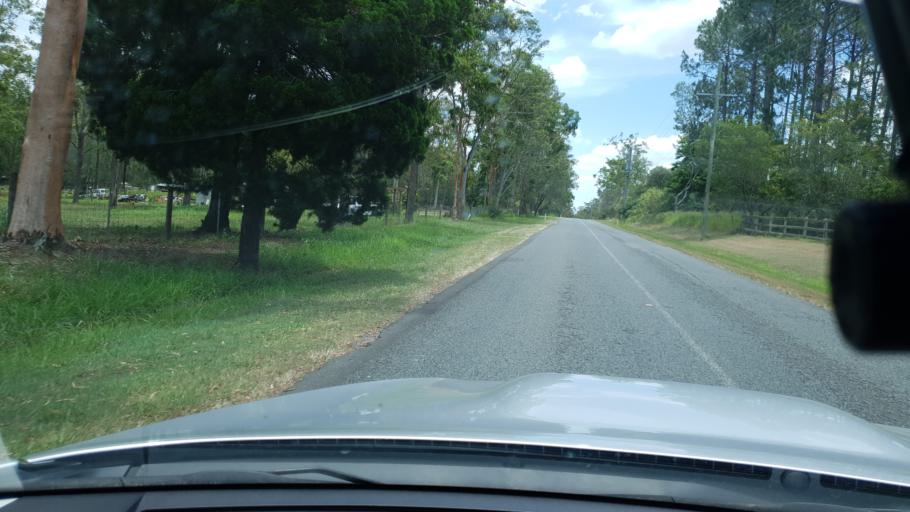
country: AU
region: Queensland
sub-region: Logan
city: North Maclean
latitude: -27.7722
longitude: 152.9911
